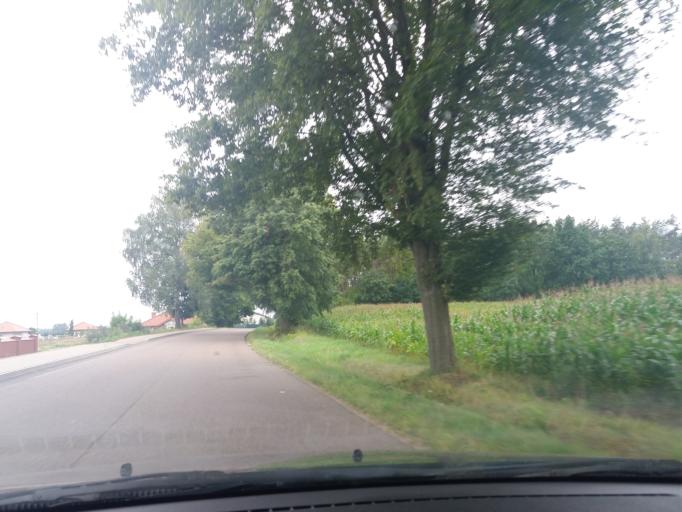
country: PL
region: Masovian Voivodeship
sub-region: Powiat mlawski
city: Wieczfnia Koscielna
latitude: 53.1999
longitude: 20.4883
